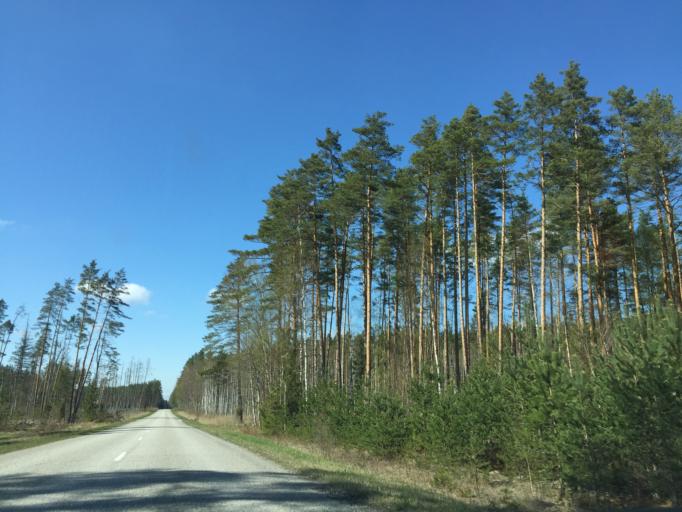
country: LV
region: Strenci
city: Seda
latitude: 57.5898
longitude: 25.7384
